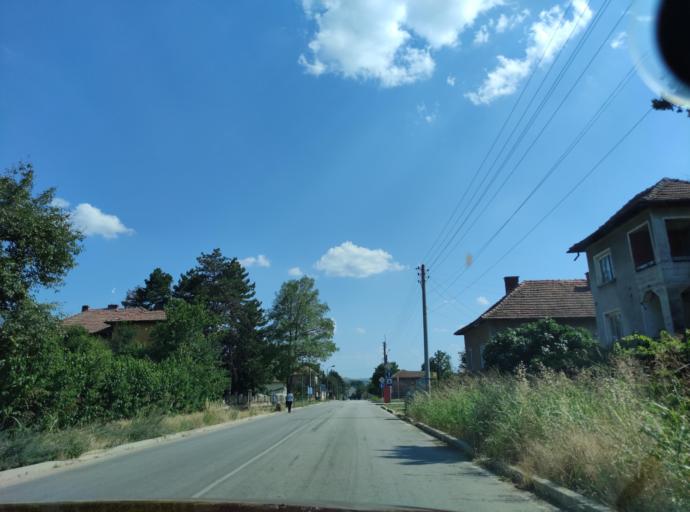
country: BG
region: Pleven
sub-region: Obshtina Cherven Bryag
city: Koynare
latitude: 43.3313
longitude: 24.0668
